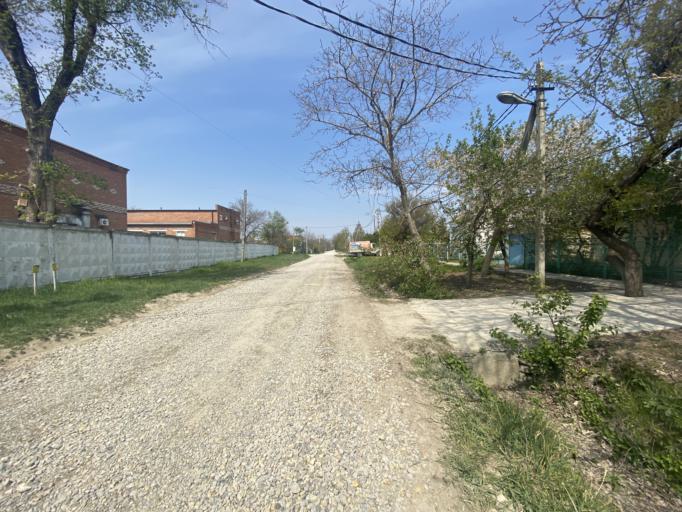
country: RU
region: Krasnodarskiy
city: Slavyansk-na-Kubani
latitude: 45.2688
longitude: 38.1218
